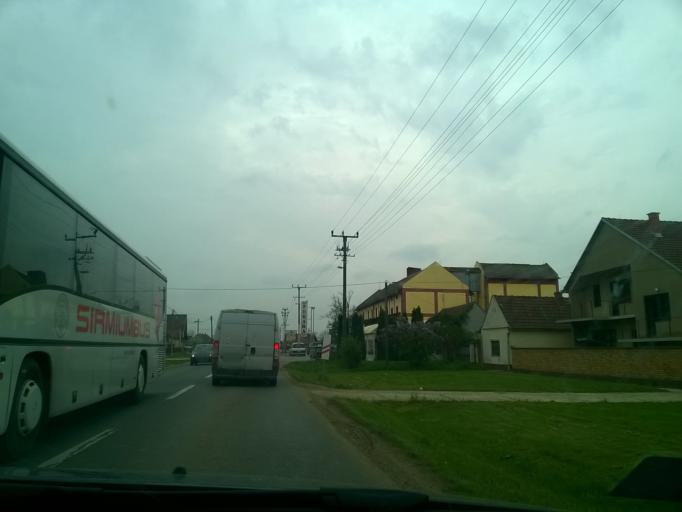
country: RS
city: Platicevo
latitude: 44.8302
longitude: 19.7768
